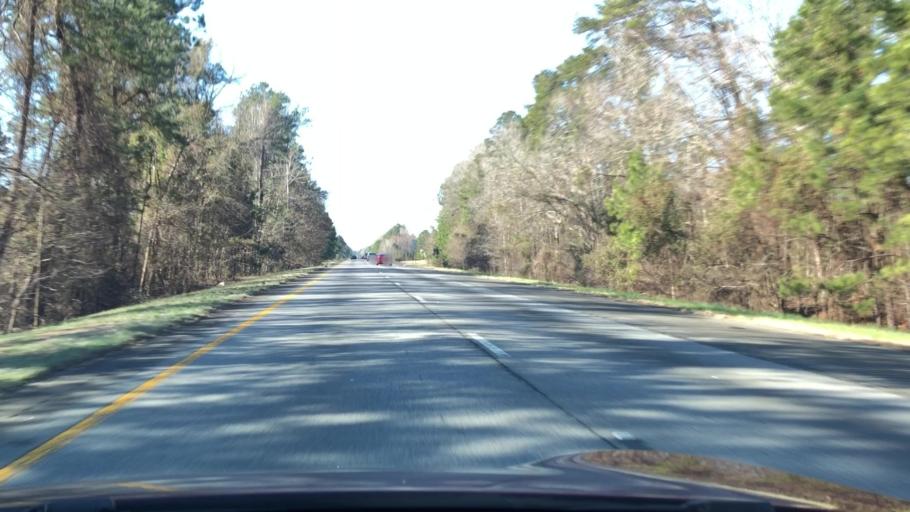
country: US
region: South Carolina
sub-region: Clarendon County
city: Manning
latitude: 33.5835
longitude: -80.3659
